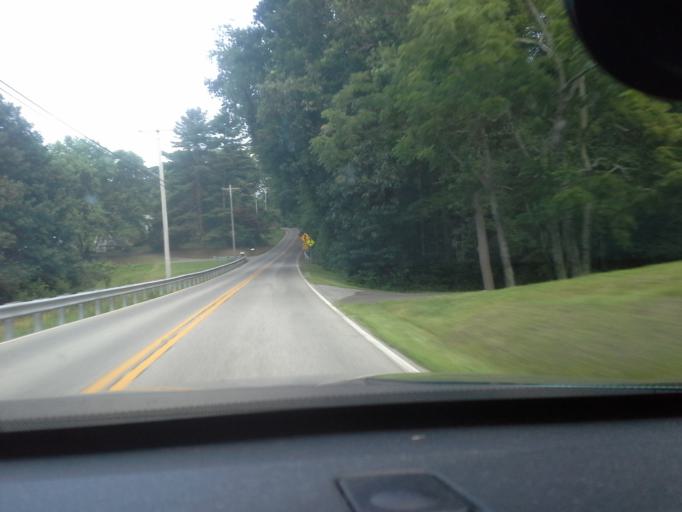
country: US
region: Maryland
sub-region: Calvert County
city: Prince Frederick
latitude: 38.5962
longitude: -76.5461
